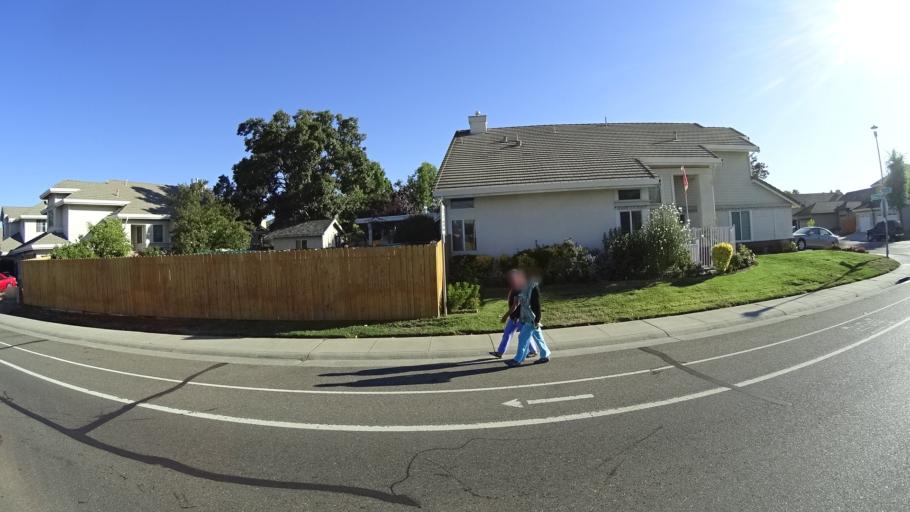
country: US
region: California
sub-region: Sacramento County
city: Elk Grove
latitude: 38.4475
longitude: -121.3846
